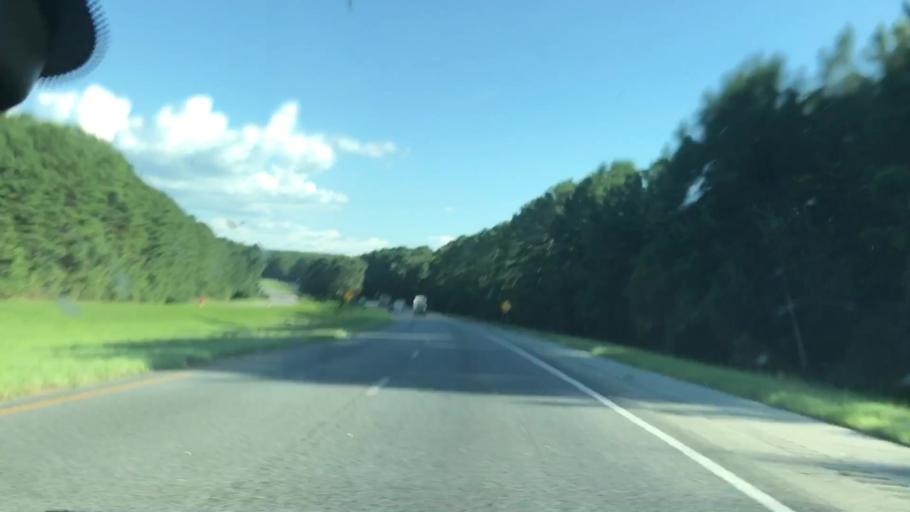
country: US
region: Georgia
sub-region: Harris County
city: Hamilton
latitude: 32.6404
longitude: -84.9697
